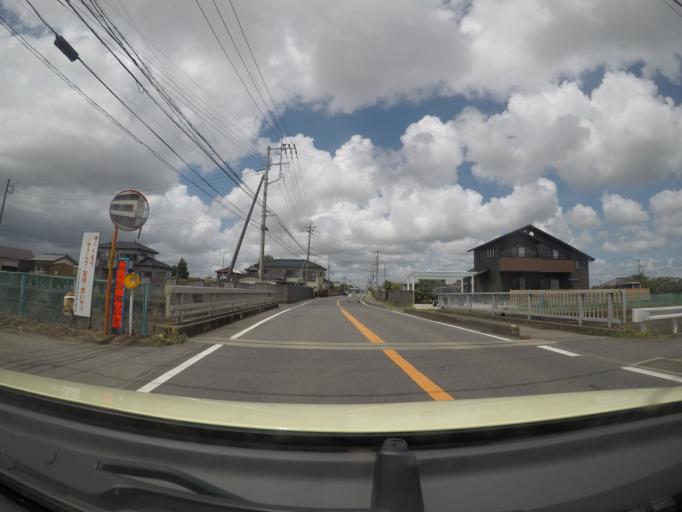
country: JP
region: Ibaraki
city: Mitsukaido
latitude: 36.0388
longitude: 139.9878
